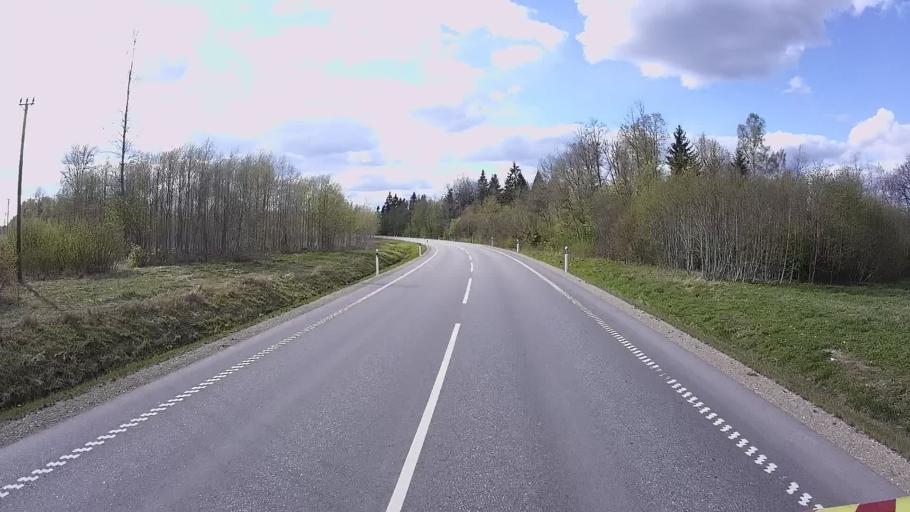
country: EE
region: Jogevamaa
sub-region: Mustvee linn
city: Mustvee
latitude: 58.8500
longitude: 26.8566
